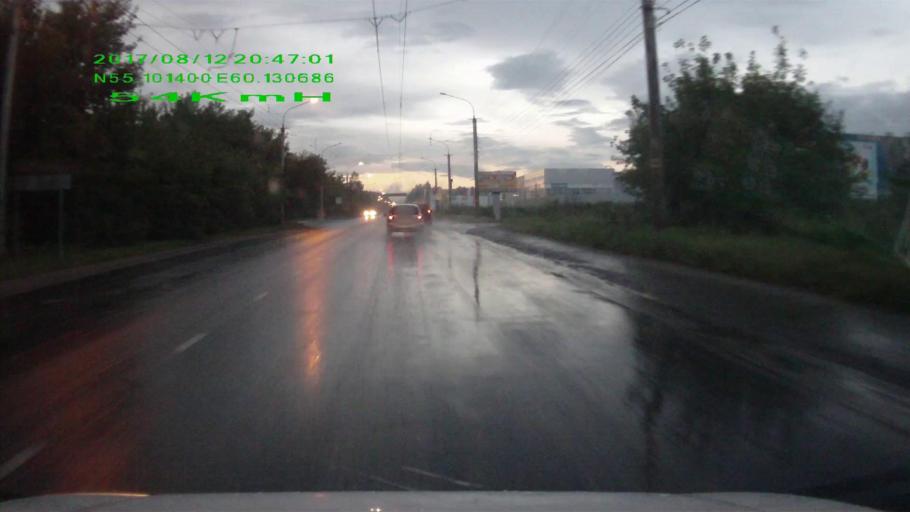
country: RU
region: Chelyabinsk
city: Turgoyak
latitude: 55.1017
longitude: 60.1307
